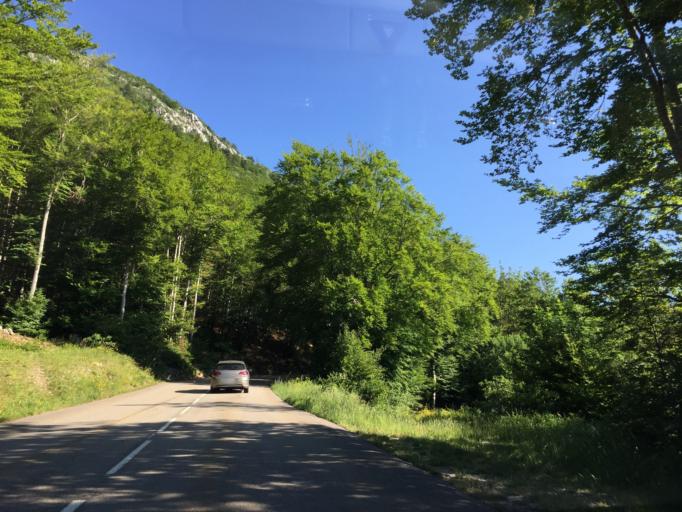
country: FR
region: Rhone-Alpes
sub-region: Departement de la Drome
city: Saint-Laurent-en-Royans
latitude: 44.9130
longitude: 5.3700
